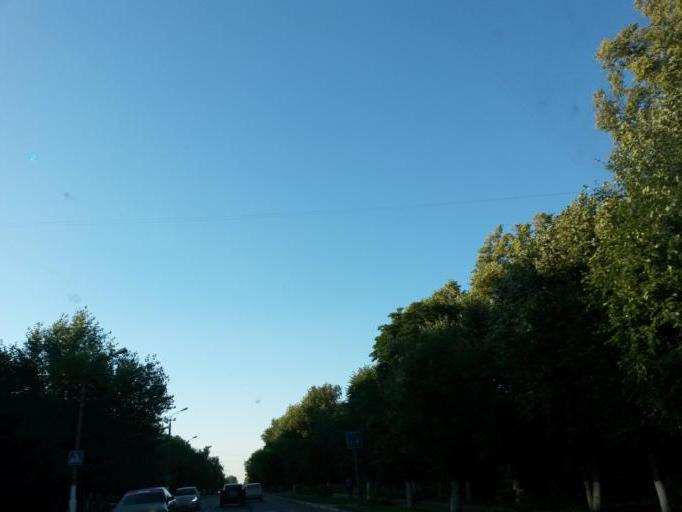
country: RU
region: Moskovskaya
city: Serpukhov
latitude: 54.9285
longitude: 37.4038
